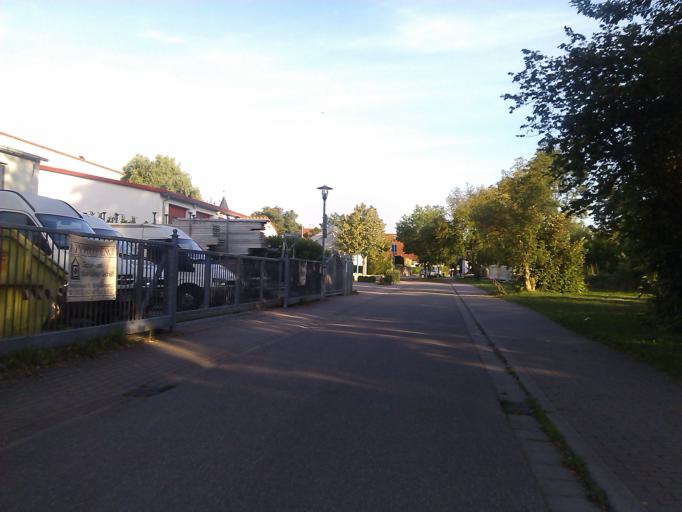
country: DE
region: Baden-Wuerttemberg
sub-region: Karlsruhe Region
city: Rauenberg
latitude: 49.2597
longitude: 8.7125
